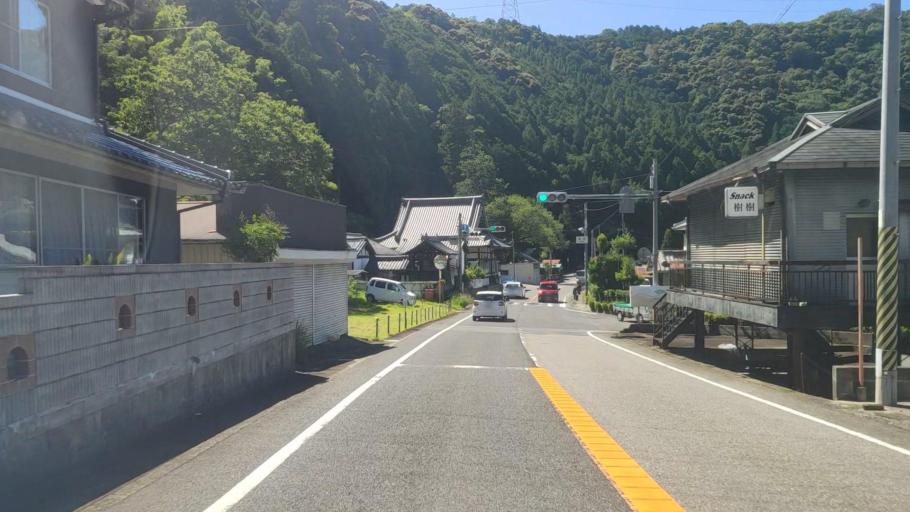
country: JP
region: Nara
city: Yoshino-cho
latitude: 34.3767
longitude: 135.9081
